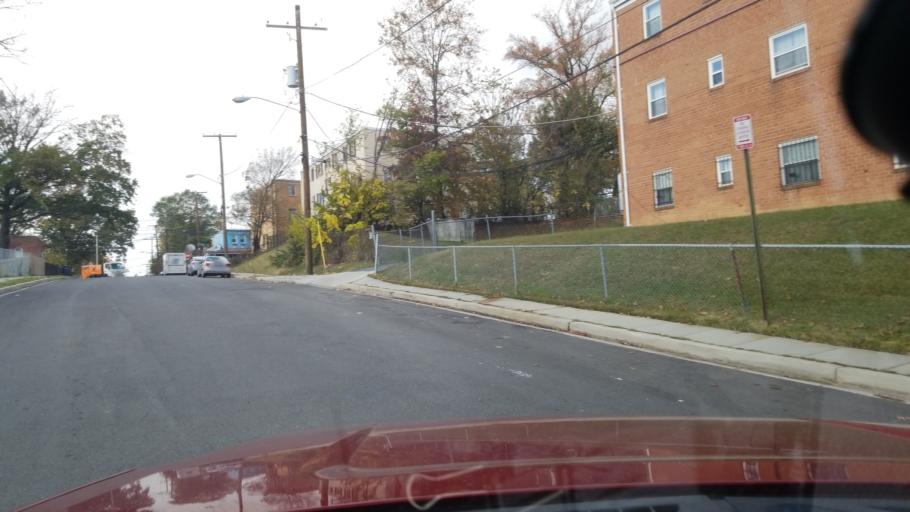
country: US
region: Maryland
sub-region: Prince George's County
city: Fairmount Heights
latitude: 38.8958
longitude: -76.9137
